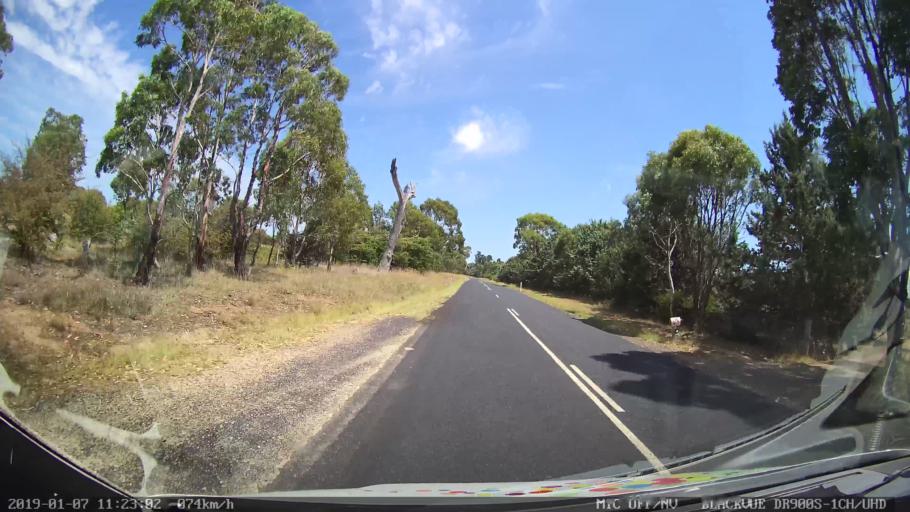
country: AU
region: New South Wales
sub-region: Armidale Dumaresq
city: Armidale
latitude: -30.4782
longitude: 151.6251
